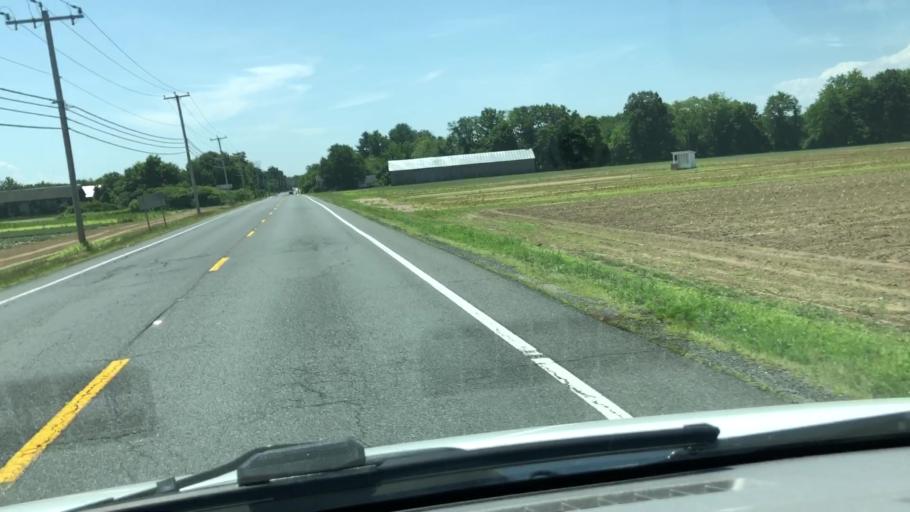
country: US
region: Massachusetts
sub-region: Franklin County
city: Whately
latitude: 42.4431
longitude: -72.6254
